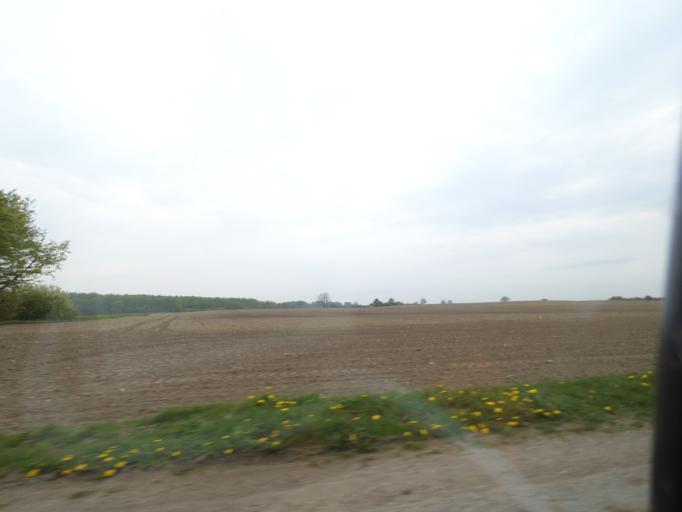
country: DK
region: South Denmark
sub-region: Faaborg-Midtfyn Kommune
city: Ringe
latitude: 55.1872
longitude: 10.5711
